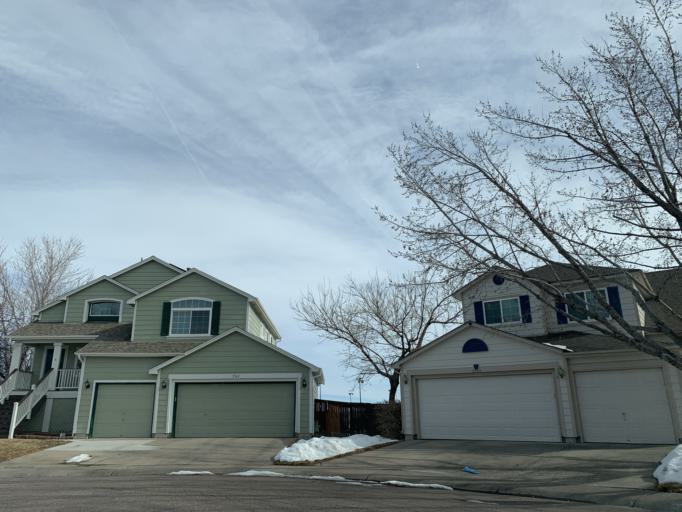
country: US
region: Colorado
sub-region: Douglas County
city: Carriage Club
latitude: 39.5415
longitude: -104.9237
